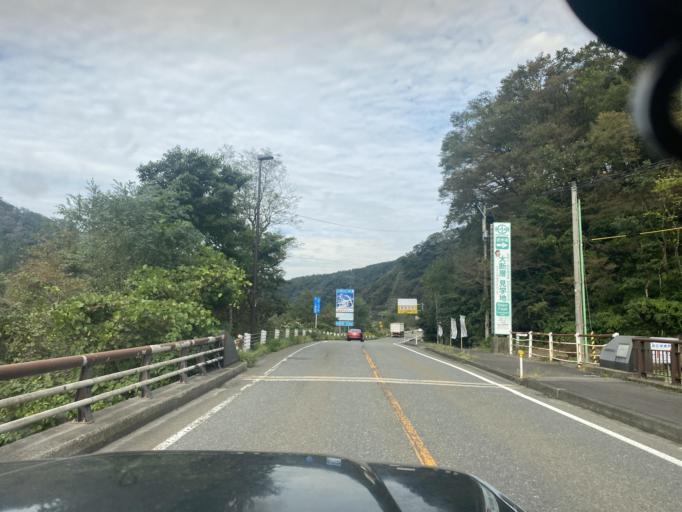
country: JP
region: Niigata
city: Itoigawa
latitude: 36.9703
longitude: 137.8676
